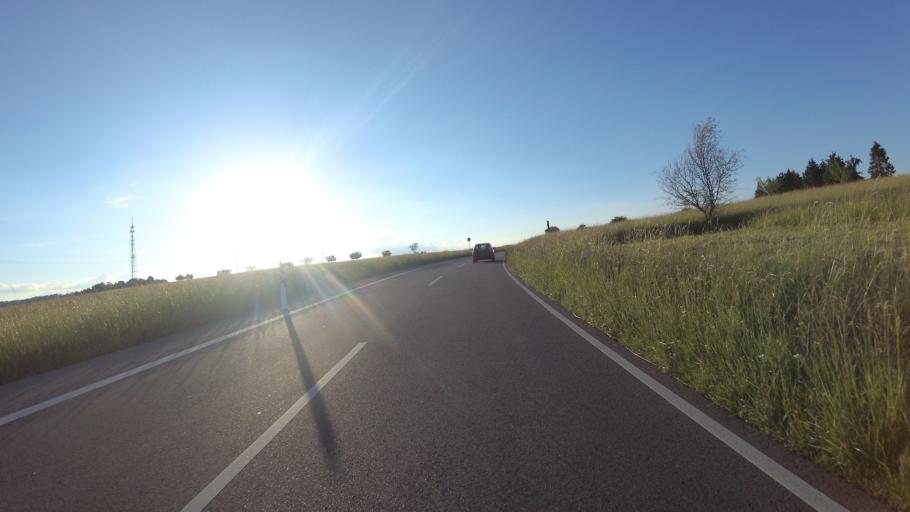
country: FR
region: Lorraine
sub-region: Departement de la Moselle
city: Sarreguemines
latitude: 49.1347
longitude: 7.0612
